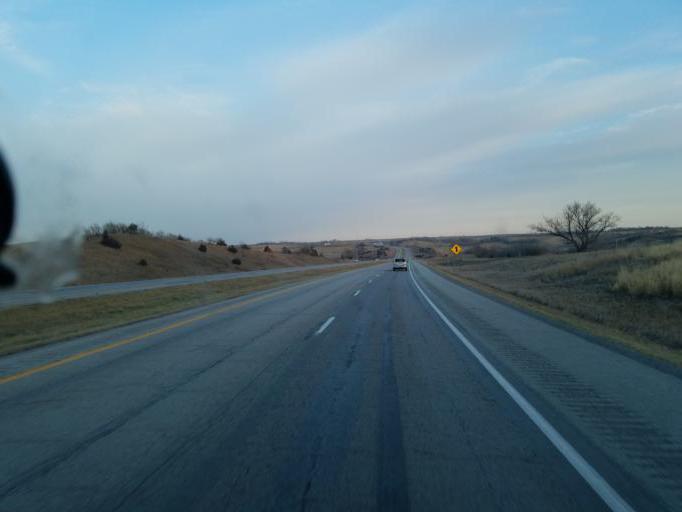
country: US
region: Iowa
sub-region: Harrison County
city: Missouri Valley
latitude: 41.4942
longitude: -95.8392
